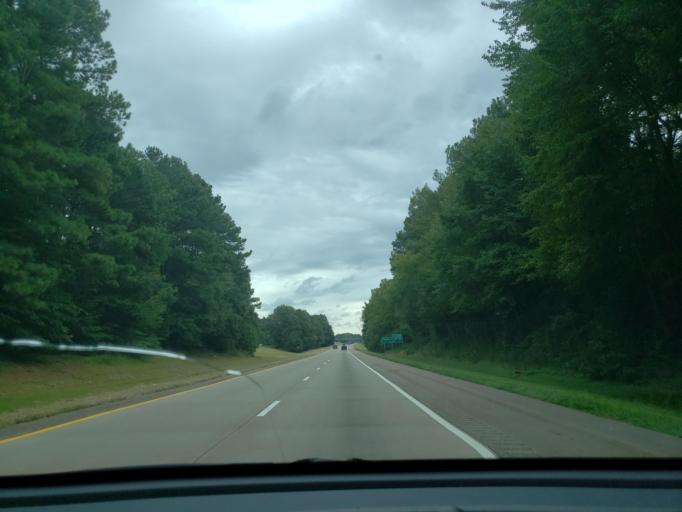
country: US
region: North Carolina
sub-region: Granville County
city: Oxford
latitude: 36.3211
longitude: -78.5000
